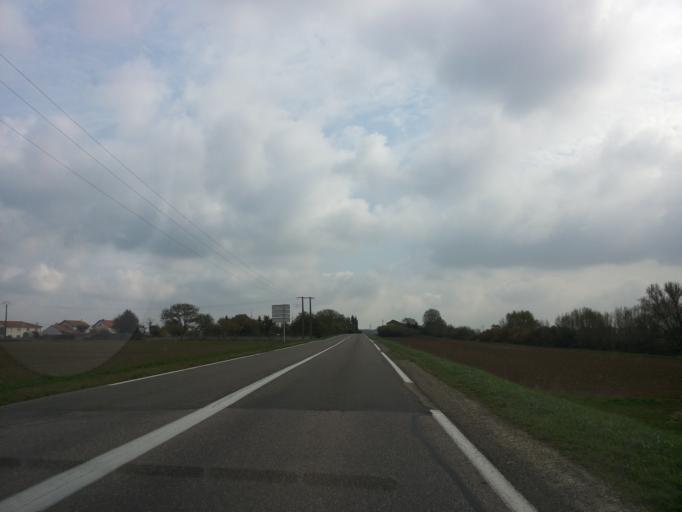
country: FR
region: Lorraine
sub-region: Departement de la Moselle
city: Chateau-Salins
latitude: 48.8669
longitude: 6.4290
